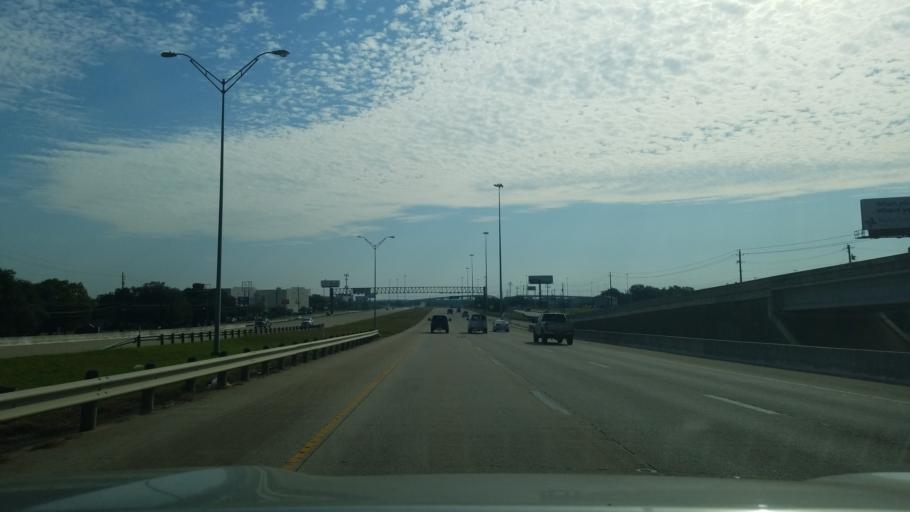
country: US
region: Texas
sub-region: Travis County
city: Barton Creek
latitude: 30.2364
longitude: -97.8372
